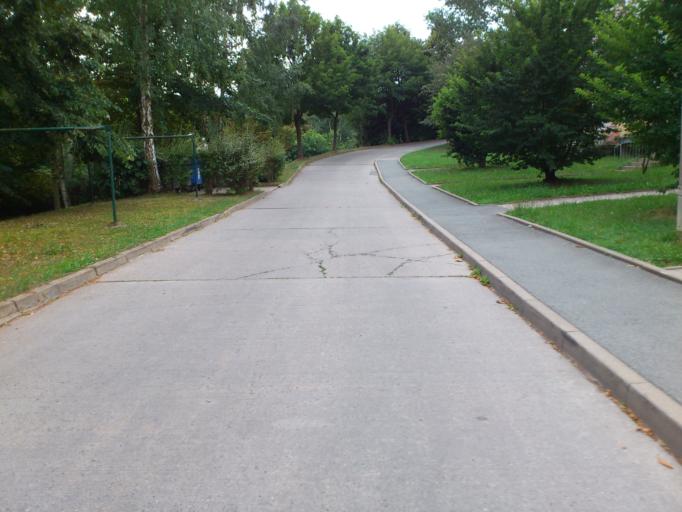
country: DE
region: Saxony
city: Neukirchen
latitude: 50.7812
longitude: 12.8772
